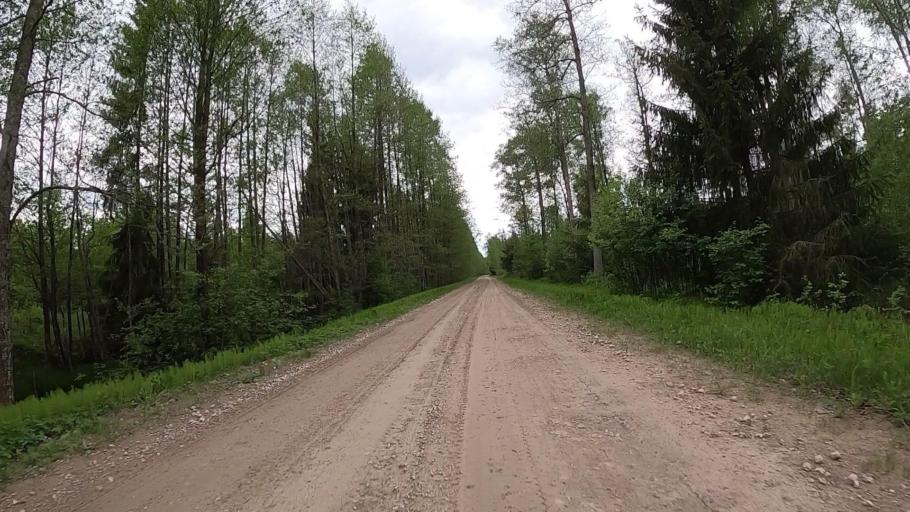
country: LV
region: Ozolnieku
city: Ozolnieki
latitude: 56.7884
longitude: 23.7755
